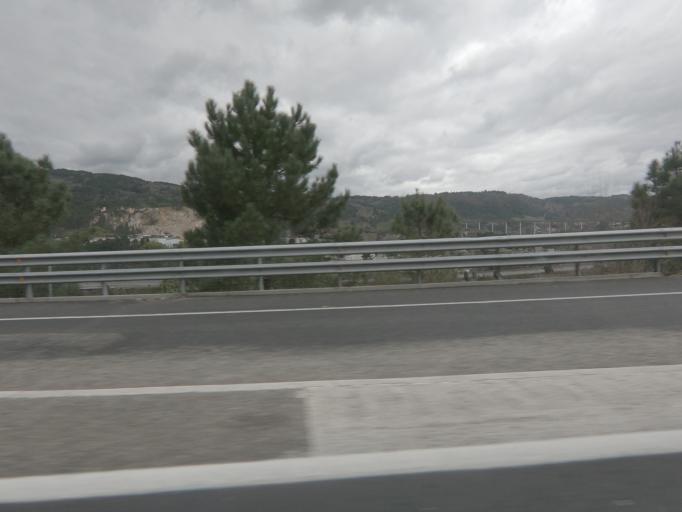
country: ES
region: Galicia
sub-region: Provincia de Ourense
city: Toen
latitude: 42.3456
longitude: -7.9166
